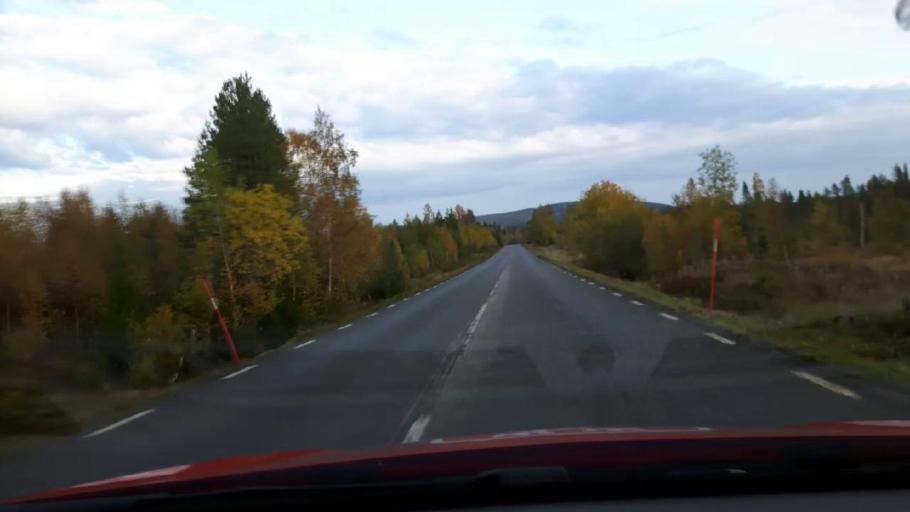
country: SE
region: Jaemtland
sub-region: OEstersunds Kommun
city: Ostersund
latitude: 63.3150
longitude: 14.6746
